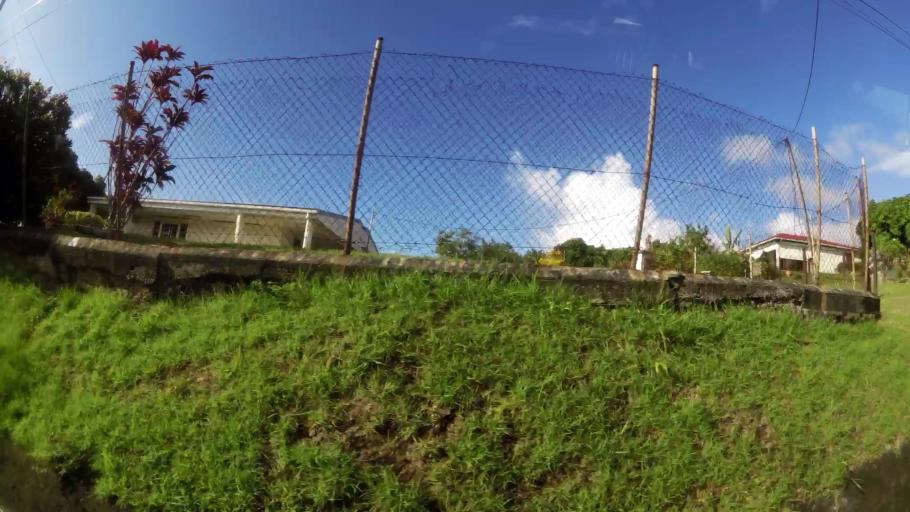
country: MQ
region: Martinique
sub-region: Martinique
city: Ducos
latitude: 14.5736
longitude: -60.9640
